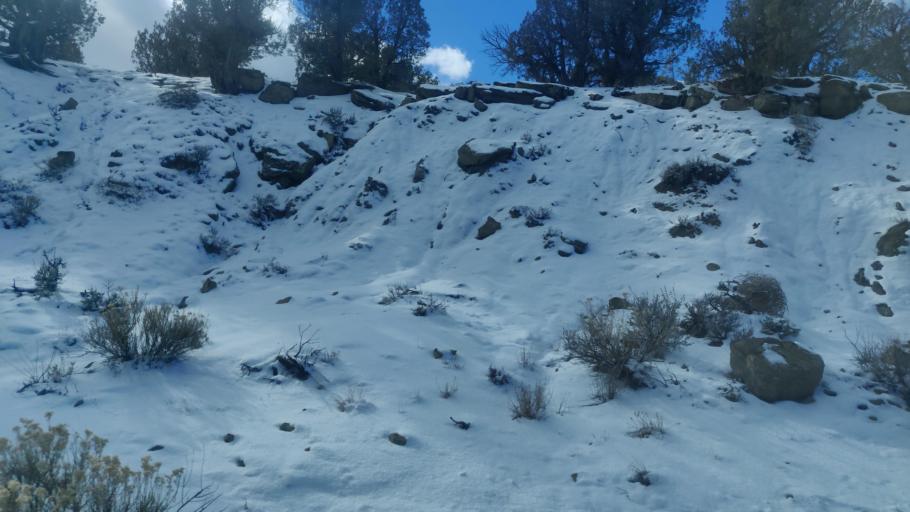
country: US
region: Colorado
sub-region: Mesa County
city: Palisade
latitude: 39.2094
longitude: -108.1461
